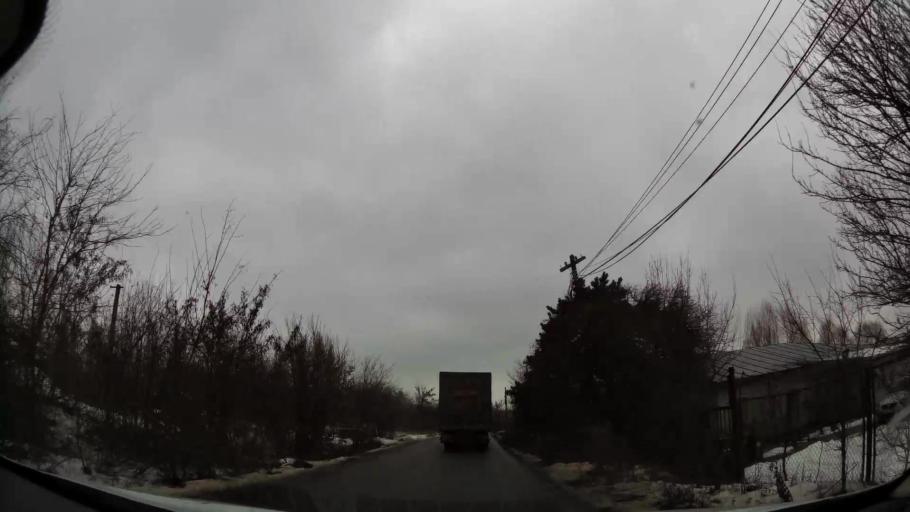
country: RO
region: Ilfov
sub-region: Comuna Chitila
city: Chitila
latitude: 44.4995
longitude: 26.0068
